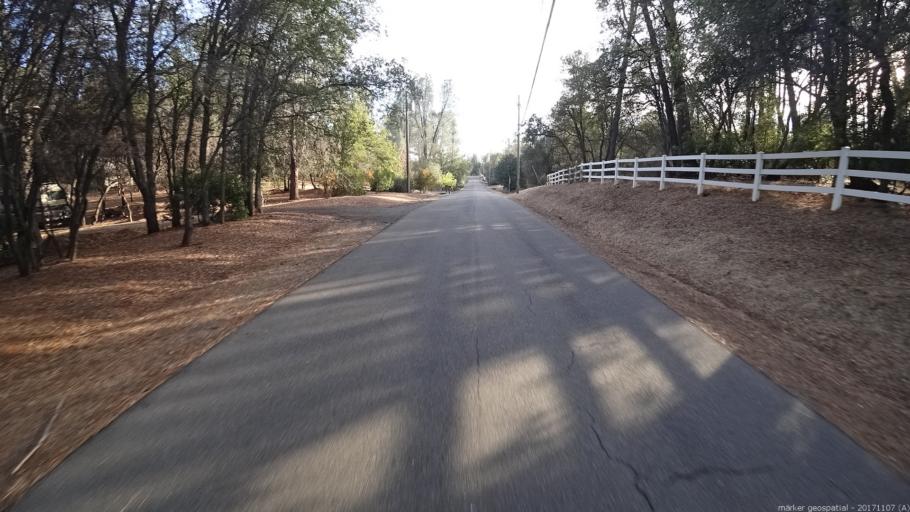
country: US
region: California
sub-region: Shasta County
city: Shasta
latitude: 40.5297
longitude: -122.4826
